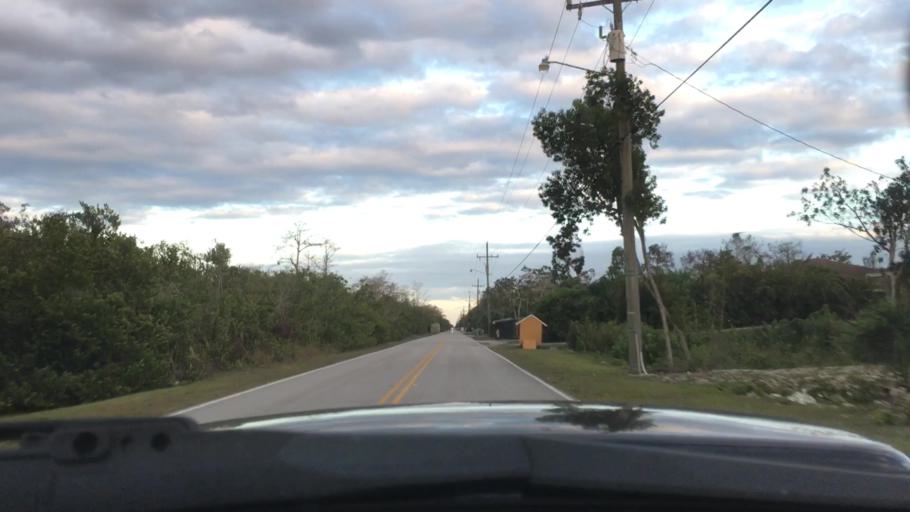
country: US
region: Florida
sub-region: Miami-Dade County
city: Kendall West
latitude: 25.7607
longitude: -80.8509
